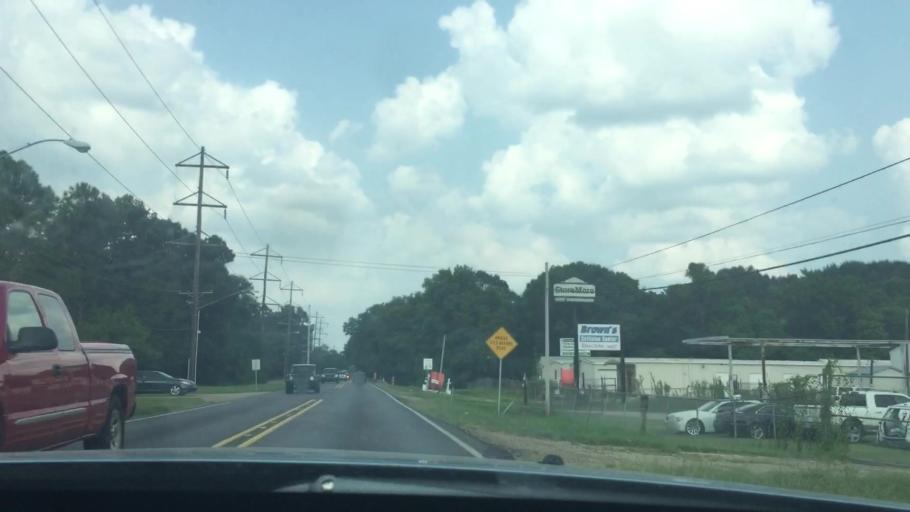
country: US
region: Louisiana
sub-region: East Baton Rouge Parish
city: Monticello
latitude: 30.4404
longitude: -91.0455
